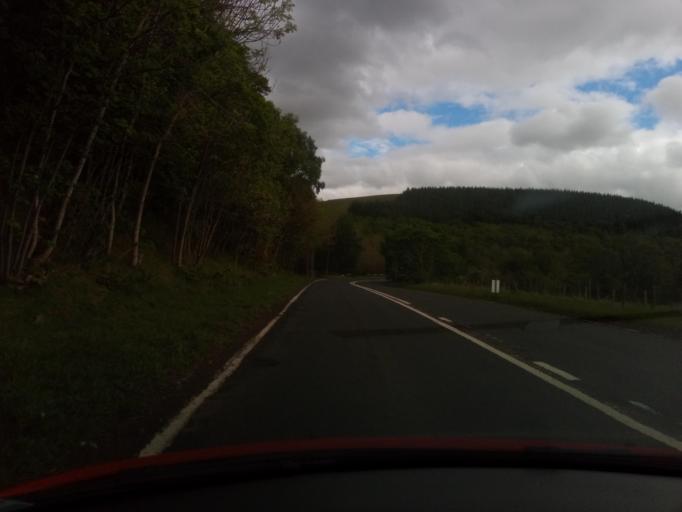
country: GB
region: Scotland
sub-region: The Scottish Borders
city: Lauder
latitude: 55.7317
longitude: -2.8903
